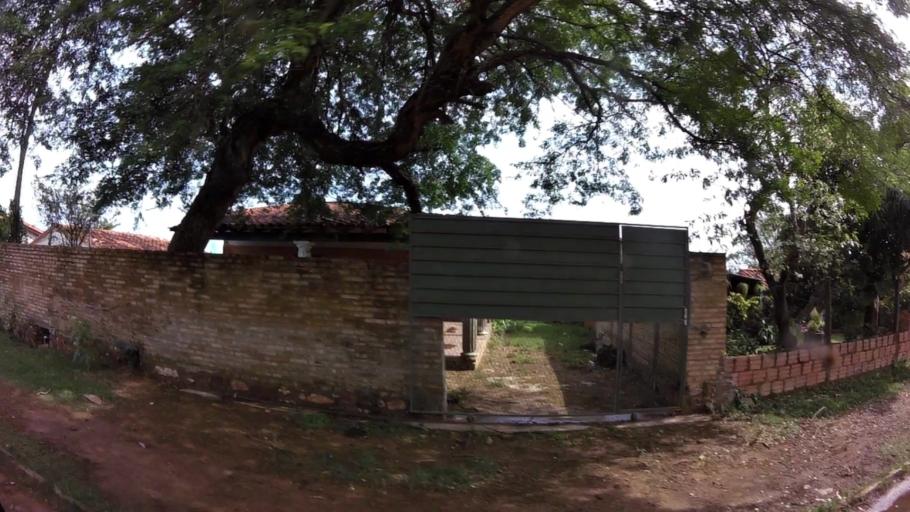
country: PY
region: Presidente Hayes
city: Villa Hayes
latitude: -25.1125
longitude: -57.4866
